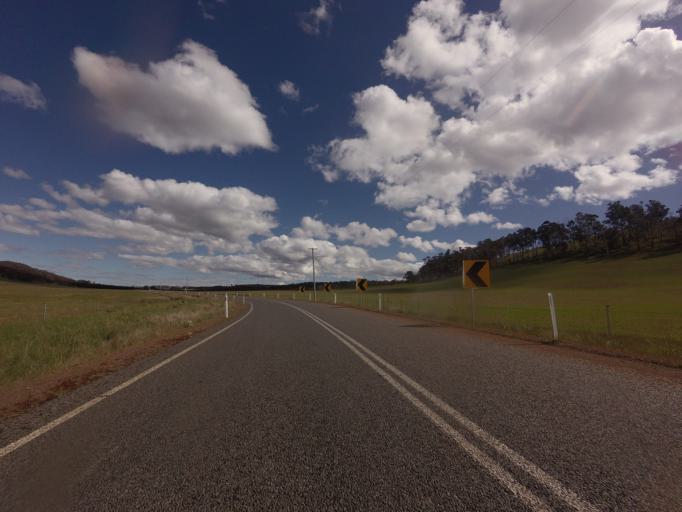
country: AU
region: Tasmania
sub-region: Brighton
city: Bridgewater
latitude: -42.4475
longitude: 147.3113
